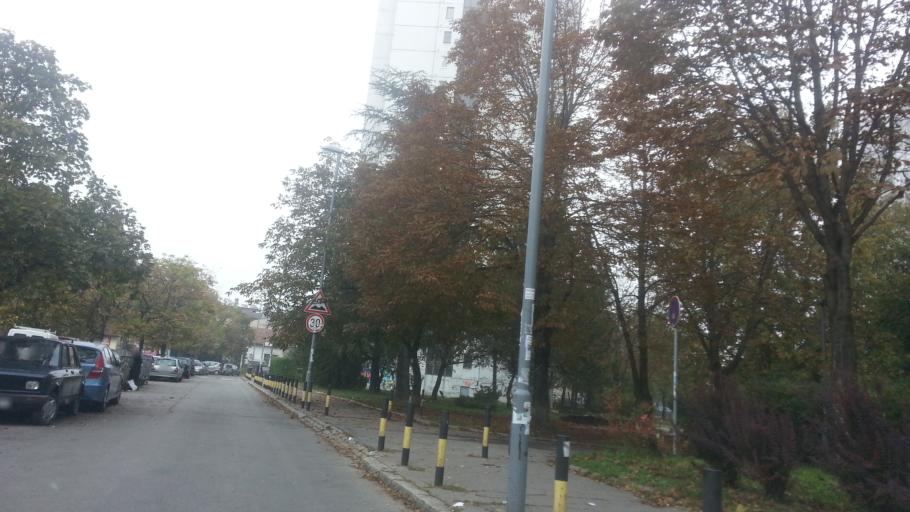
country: RS
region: Central Serbia
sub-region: Belgrade
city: Zemun
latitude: 44.8395
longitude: 20.4161
